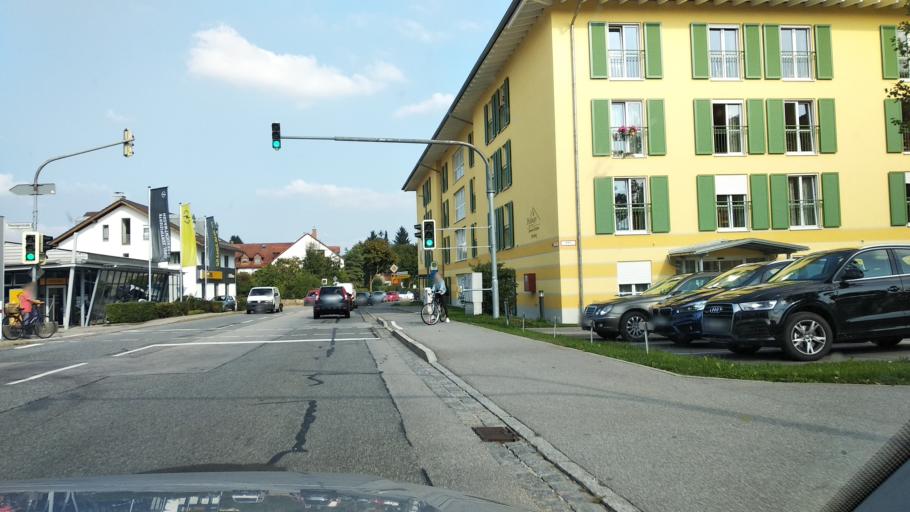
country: DE
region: Bavaria
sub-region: Upper Bavaria
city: Ebersberg
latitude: 48.0760
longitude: 11.9623
